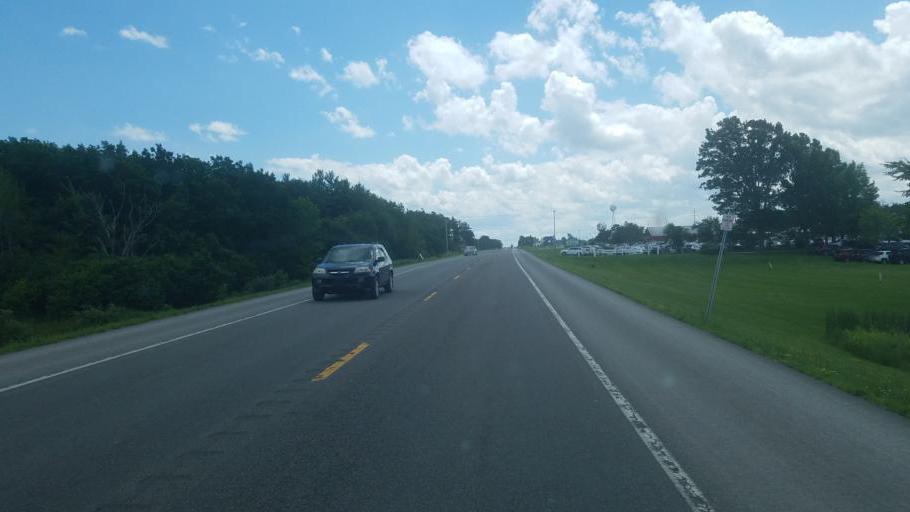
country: US
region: New York
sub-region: Yates County
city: Keuka Park
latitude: 42.5772
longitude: -77.0360
